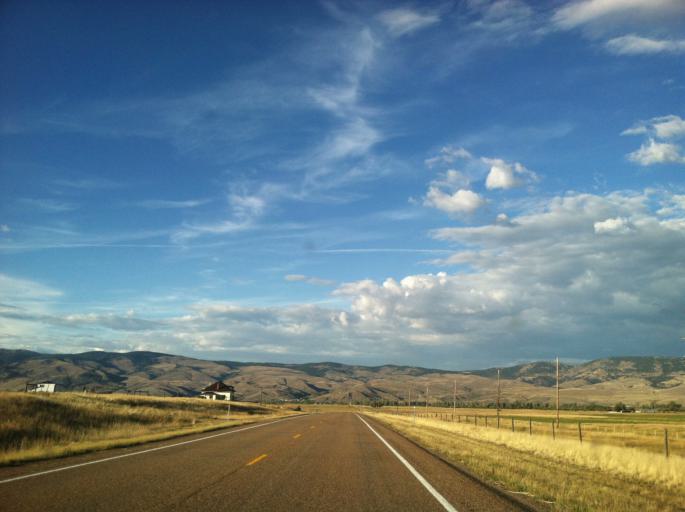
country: US
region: Montana
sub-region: Granite County
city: Philipsburg
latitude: 46.6225
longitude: -113.1716
